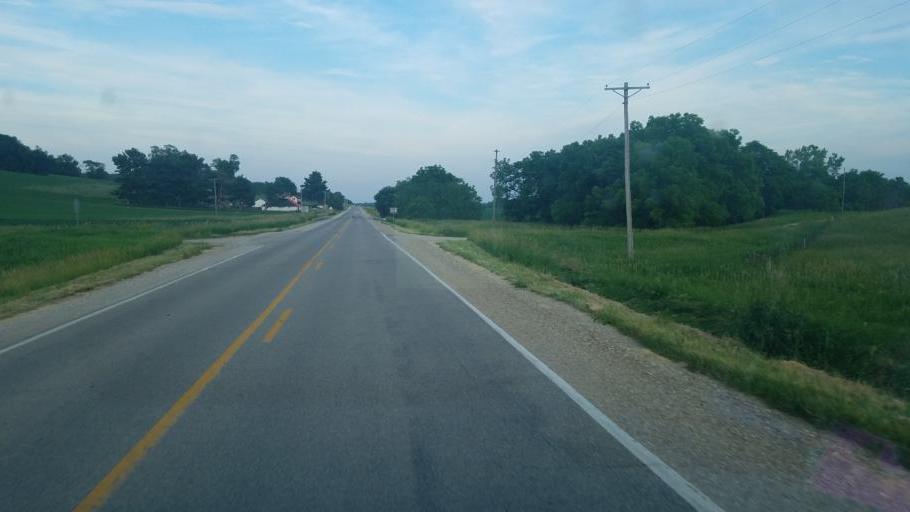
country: US
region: Iowa
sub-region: Benton County
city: Belle Plaine
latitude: 41.9121
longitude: -92.3473
